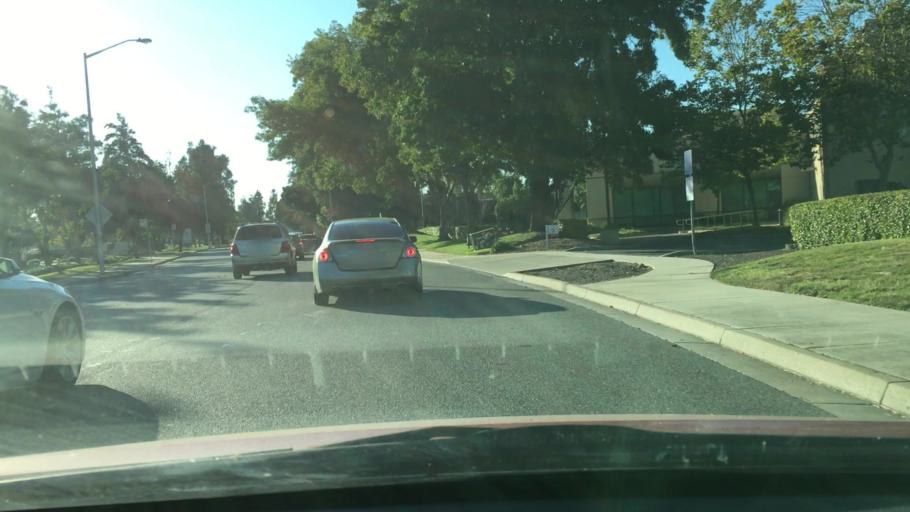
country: US
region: California
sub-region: Santa Clara County
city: Milpitas
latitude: 37.4566
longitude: -121.9176
